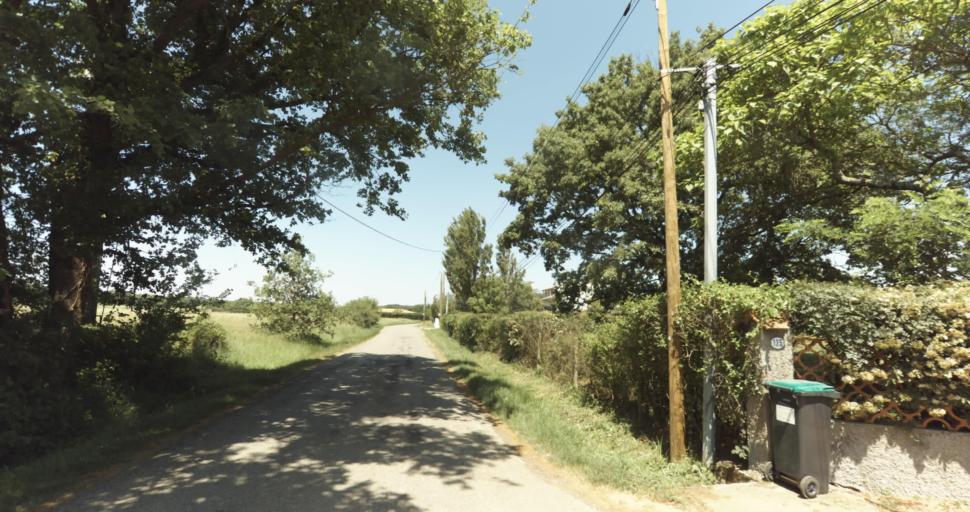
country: FR
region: Midi-Pyrenees
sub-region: Departement de la Haute-Garonne
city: Levignac
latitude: 43.6365
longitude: 1.1878
